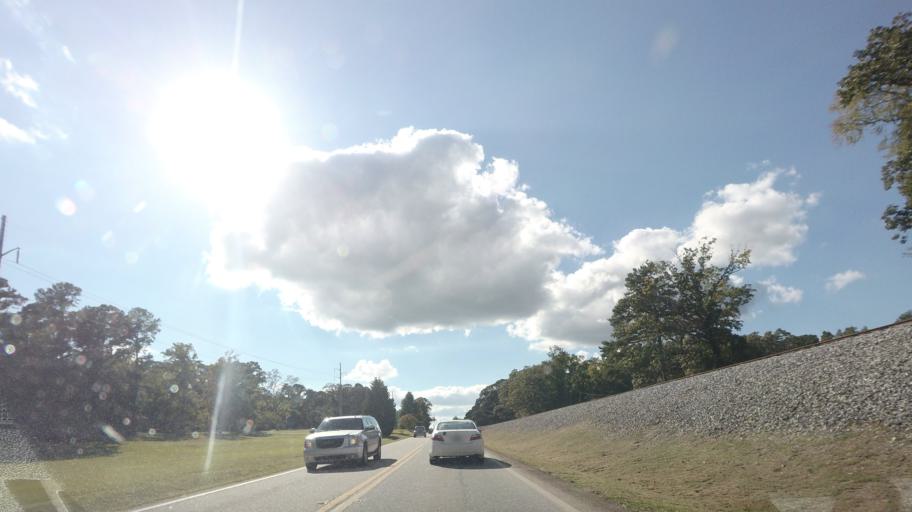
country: US
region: Georgia
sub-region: Monroe County
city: Forsyth
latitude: 33.0537
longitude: -84.0428
